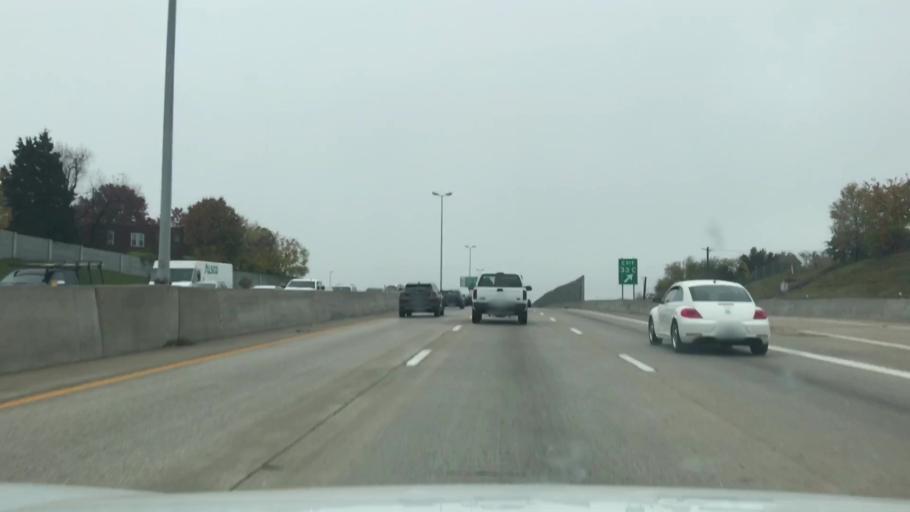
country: US
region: Missouri
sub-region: Saint Louis County
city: Richmond Heights
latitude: 38.6316
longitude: -90.3033
